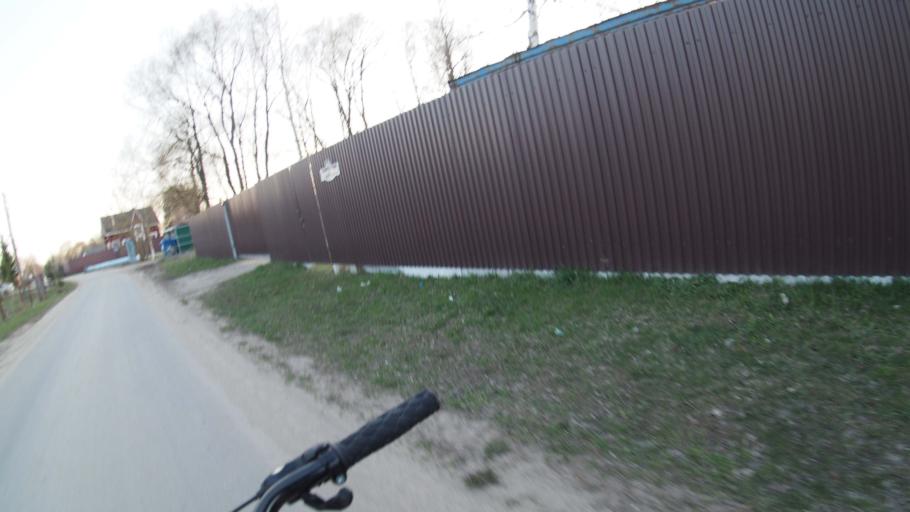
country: RU
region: Moskovskaya
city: Ramenskoye
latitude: 55.5685
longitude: 38.2942
